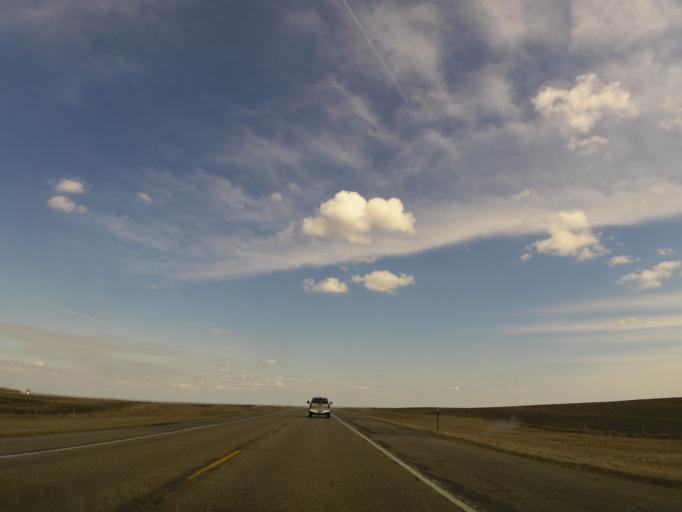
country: US
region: South Dakota
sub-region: Deuel County
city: Clear Lake
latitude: 44.9332
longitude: -96.6090
